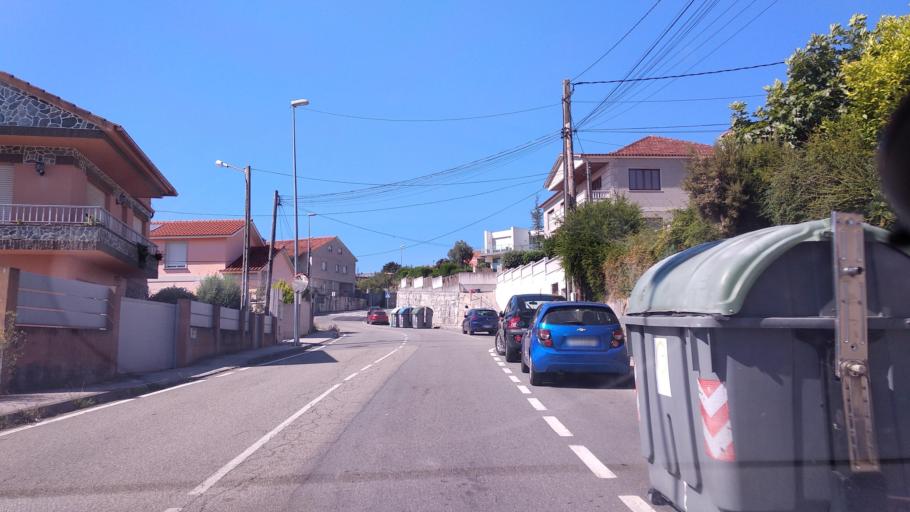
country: ES
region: Galicia
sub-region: Provincia de Pontevedra
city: Moana
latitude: 42.2759
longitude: -8.7679
